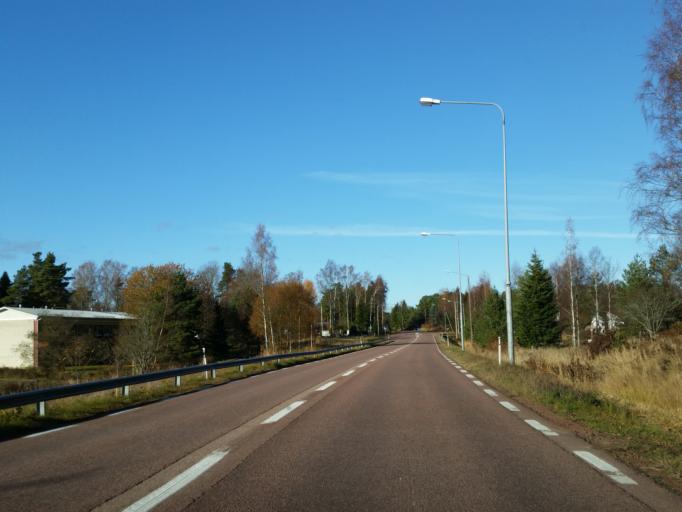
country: AX
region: Alands landsbygd
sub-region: Finstroem
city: Finstroem
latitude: 60.2327
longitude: 19.9833
